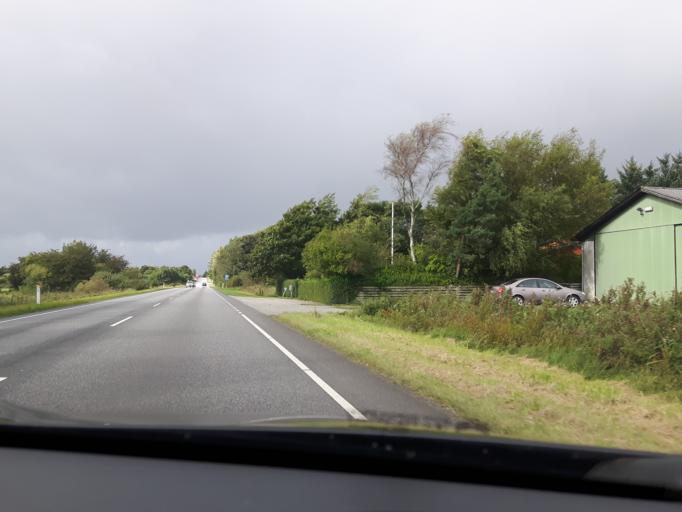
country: DK
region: North Denmark
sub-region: Jammerbugt Kommune
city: Fjerritslev
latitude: 57.0884
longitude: 9.3567
